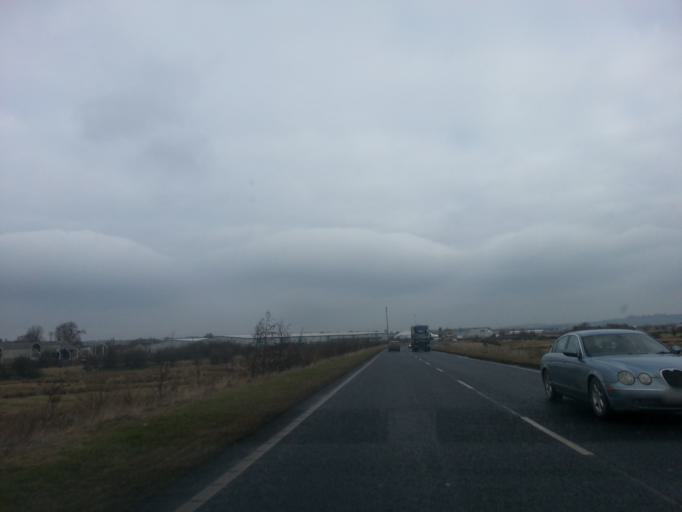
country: GB
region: England
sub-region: County Durham
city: Bishop Auckland
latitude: 54.6332
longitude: -1.7027
